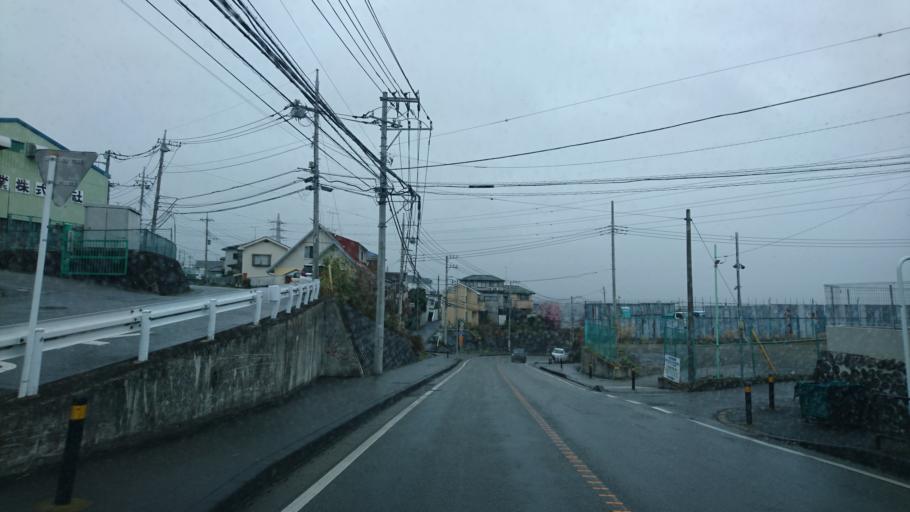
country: JP
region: Kanagawa
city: Zama
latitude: 35.5324
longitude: 139.3317
